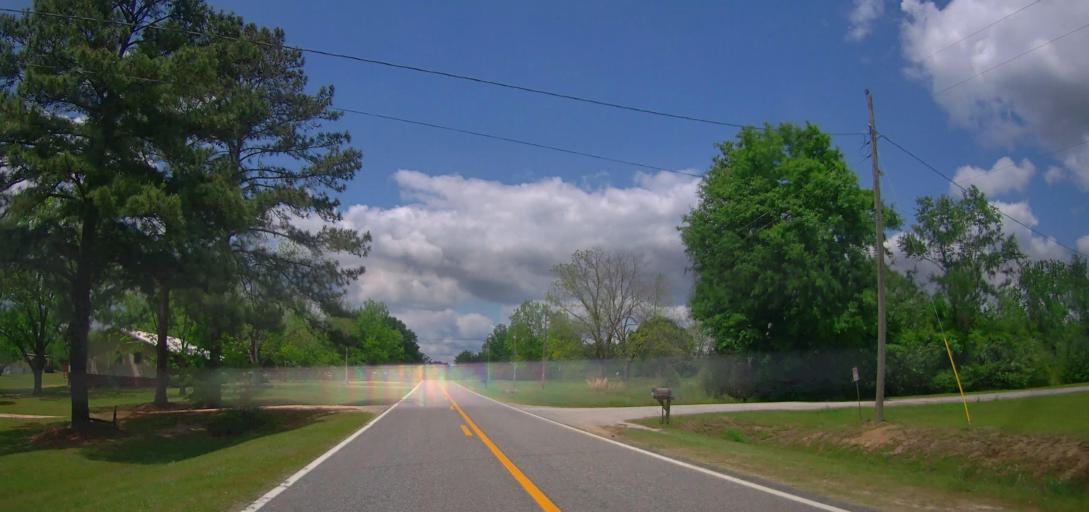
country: US
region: Georgia
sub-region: Laurens County
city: East Dublin
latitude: 32.5572
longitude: -82.8182
